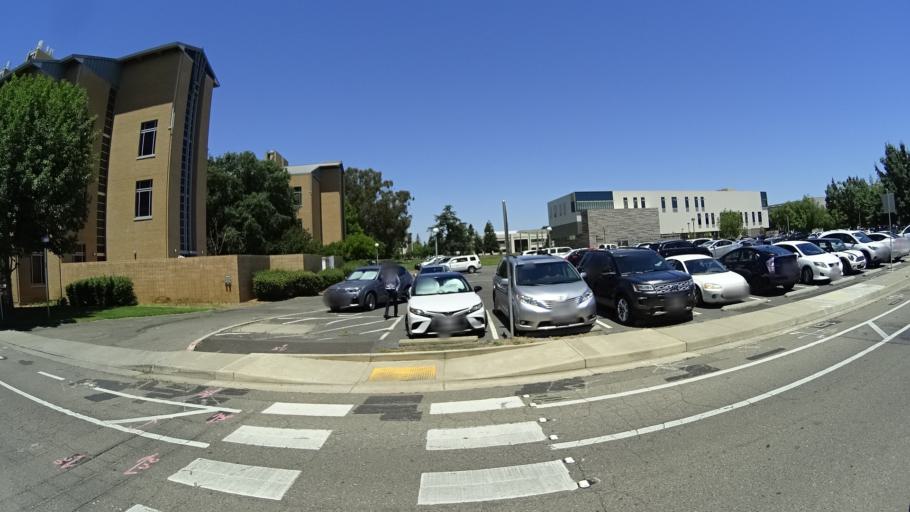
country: US
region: California
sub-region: Sacramento County
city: Sacramento
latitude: 38.5510
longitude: -121.4520
